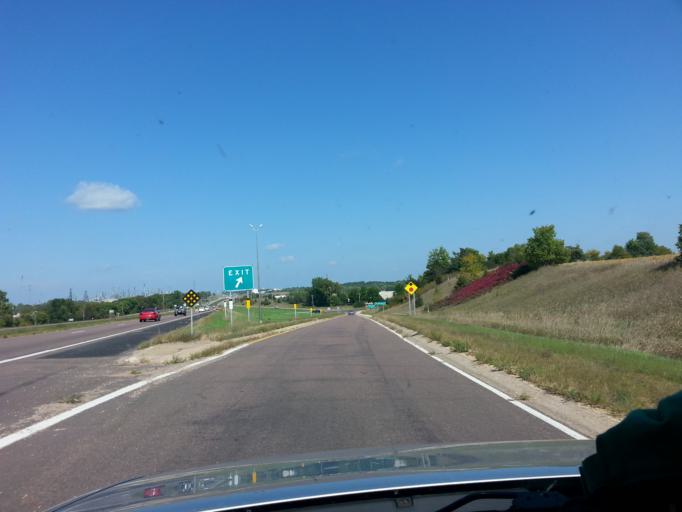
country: US
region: Minnesota
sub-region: Dakota County
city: Rosemount
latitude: 44.7362
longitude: -93.0347
